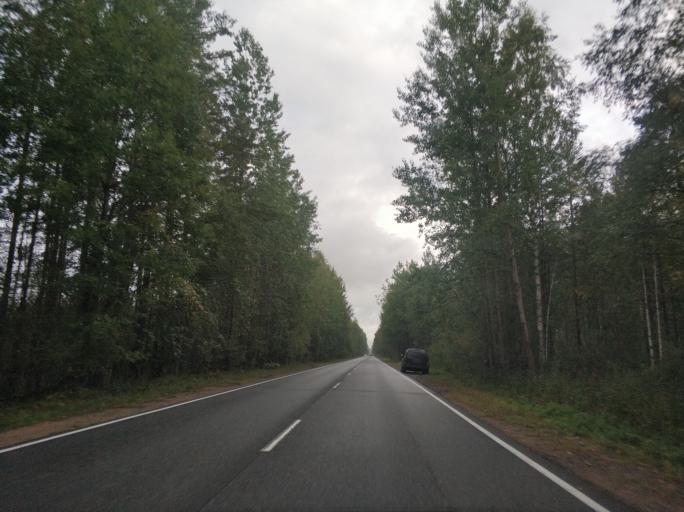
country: RU
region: Leningrad
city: Borisova Griva
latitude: 60.1462
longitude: 30.9438
